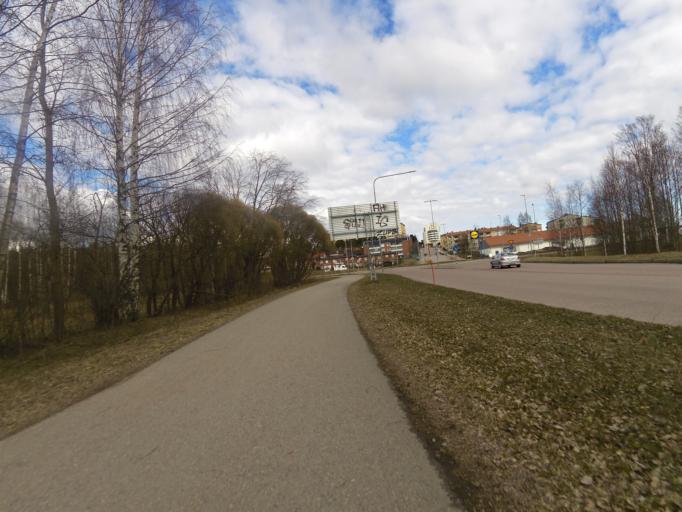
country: SE
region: Gaevleborg
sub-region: Gavle Kommun
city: Gavle
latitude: 60.6924
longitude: 17.1483
